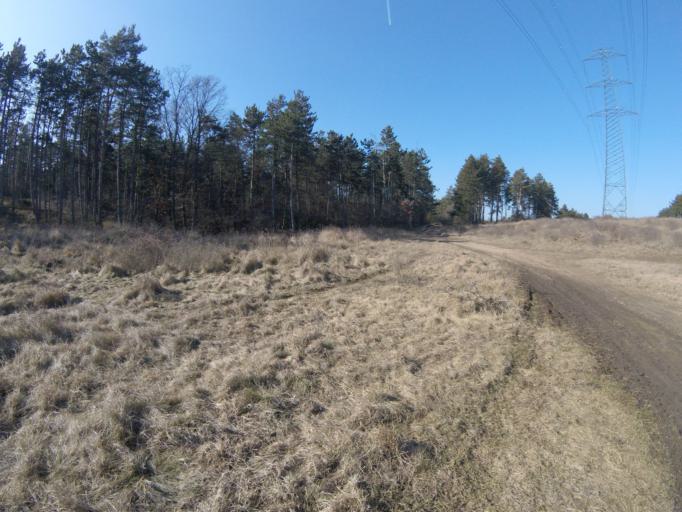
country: HU
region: Komarom-Esztergom
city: Oroszlany
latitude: 47.4591
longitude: 18.3600
